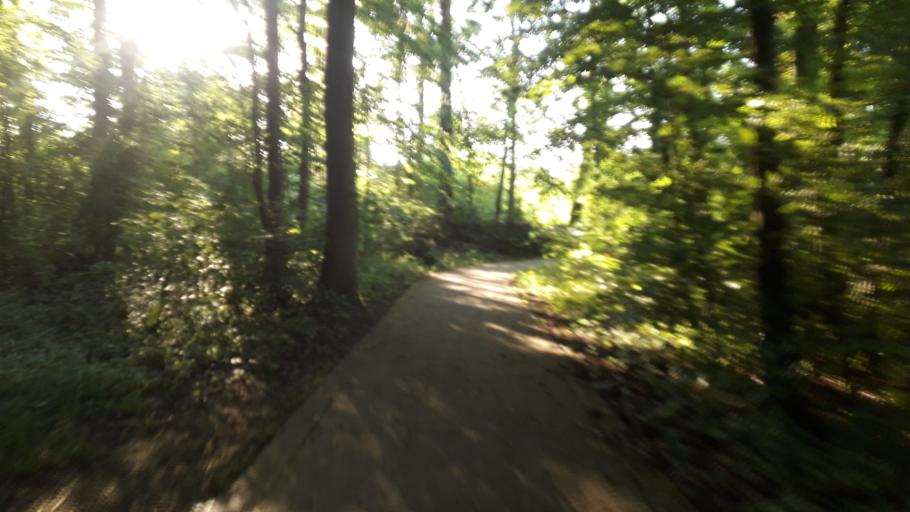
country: DE
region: North Rhine-Westphalia
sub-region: Regierungsbezirk Detmold
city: Paderborn
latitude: 51.6617
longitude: 8.7796
